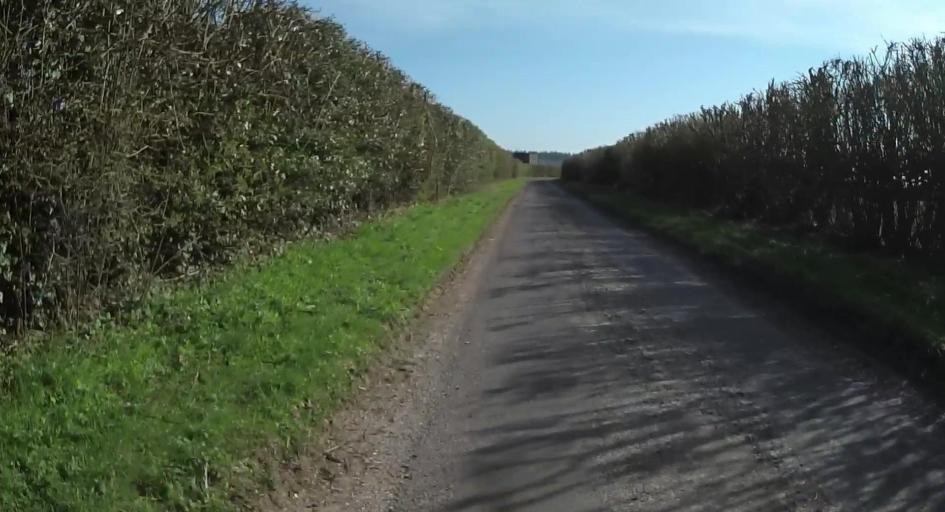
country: GB
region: England
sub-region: Hampshire
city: Highclere
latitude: 51.2498
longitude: -1.3674
